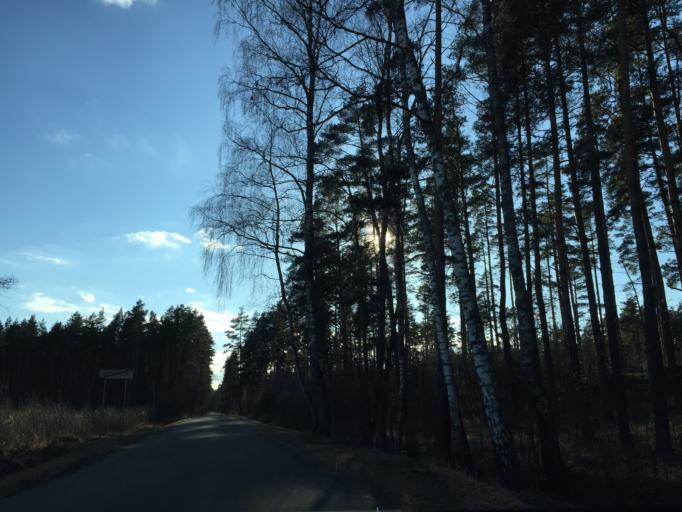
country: LV
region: Babite
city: Pinki
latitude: 56.9255
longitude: 23.8974
